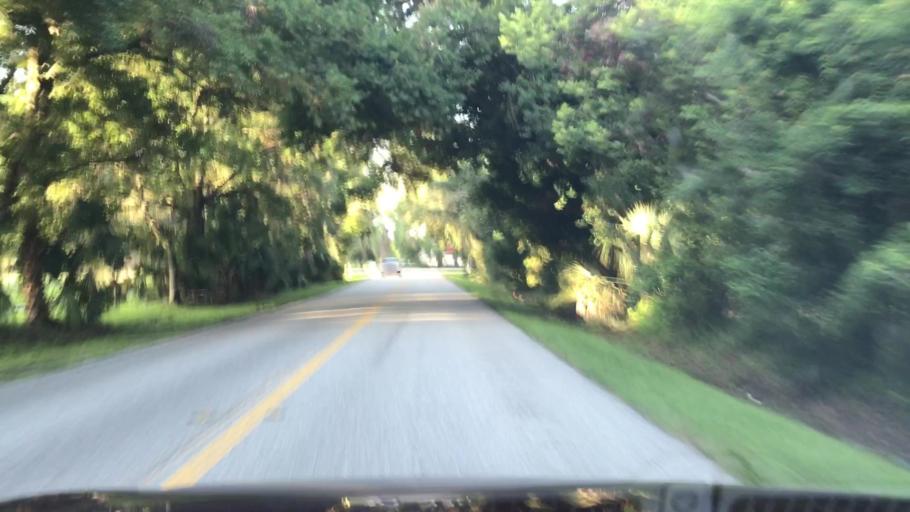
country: US
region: Florida
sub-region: Sarasota County
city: Fruitville
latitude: 27.3350
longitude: -82.4053
